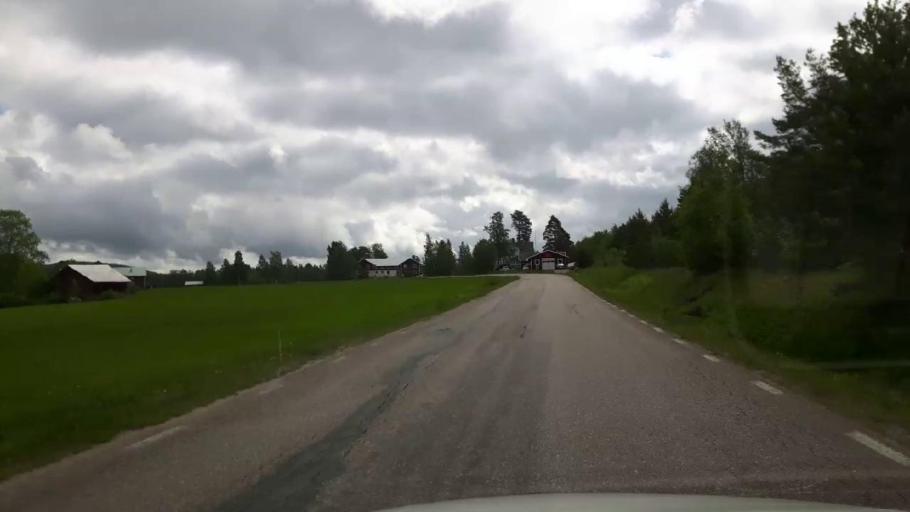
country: SE
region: Gaevleborg
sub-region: Ovanakers Kommun
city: Edsbyn
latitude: 61.3555
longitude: 15.9062
